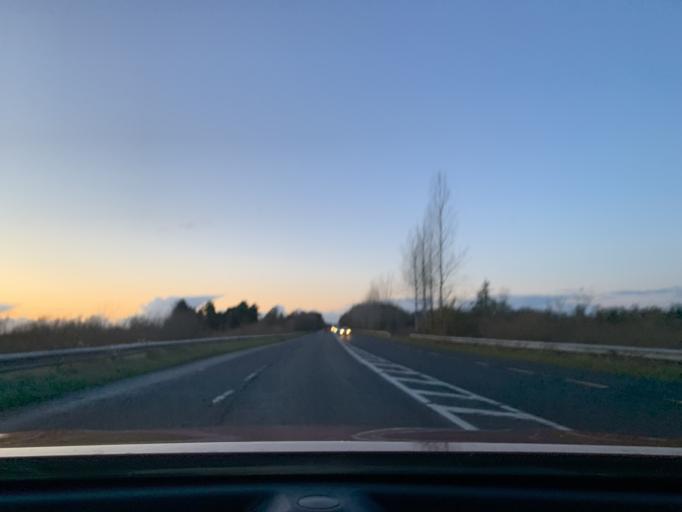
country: IE
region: Connaught
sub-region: County Leitrim
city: Carrick-on-Shannon
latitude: 53.9339
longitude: -8.0460
